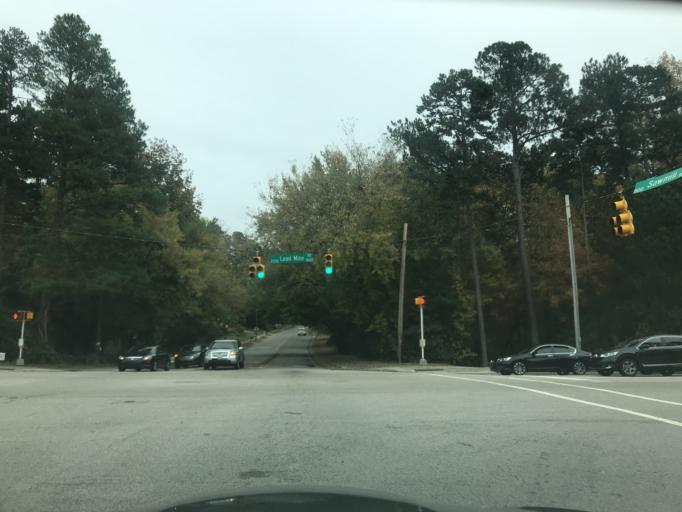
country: US
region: North Carolina
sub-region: Wake County
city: West Raleigh
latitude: 35.8847
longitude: -78.6604
